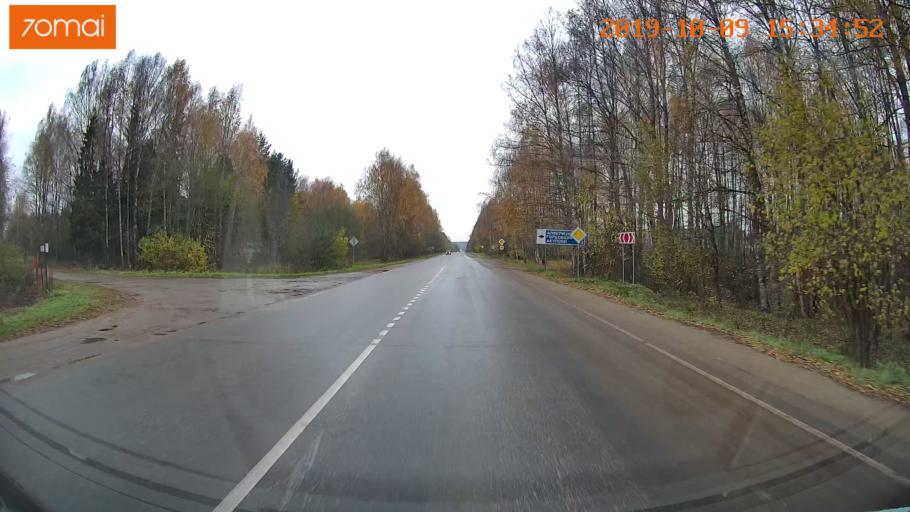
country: RU
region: Kostroma
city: Oktyabr'skiy
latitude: 57.9374
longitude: 41.2378
